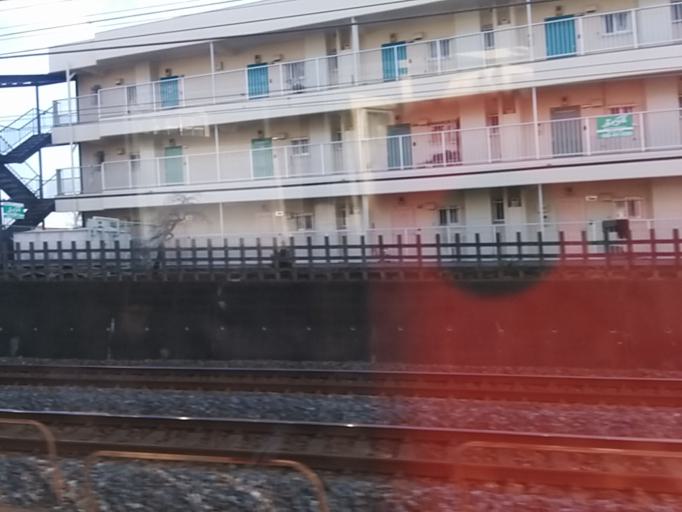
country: JP
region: Saitama
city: Asaka
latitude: 35.8046
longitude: 139.5978
